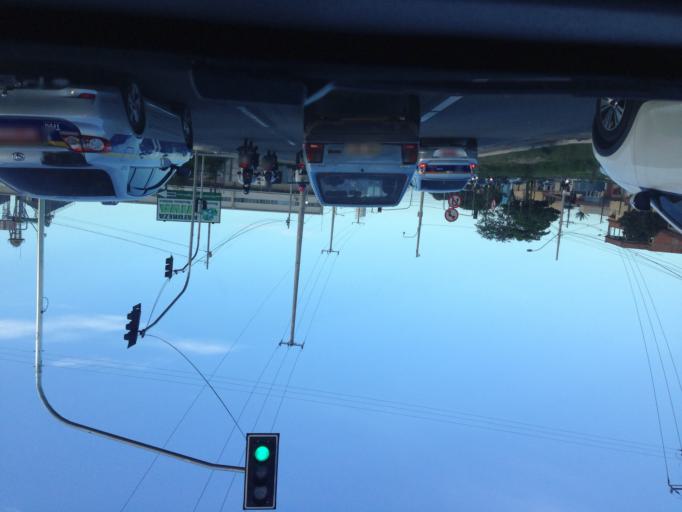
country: BR
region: Espirito Santo
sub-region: Vitoria
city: Vitoria
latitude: -20.3844
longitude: -40.3325
